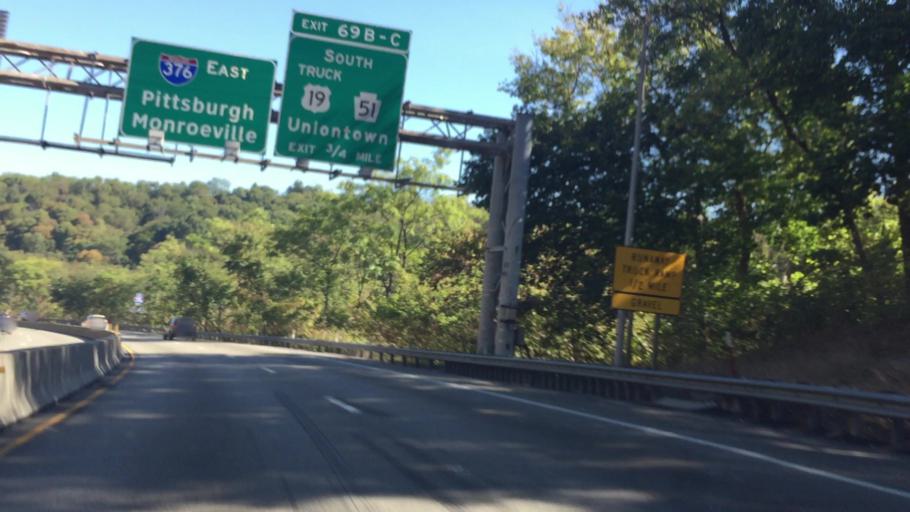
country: US
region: Pennsylvania
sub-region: Allegheny County
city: Green Tree
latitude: 40.4210
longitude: -80.0315
